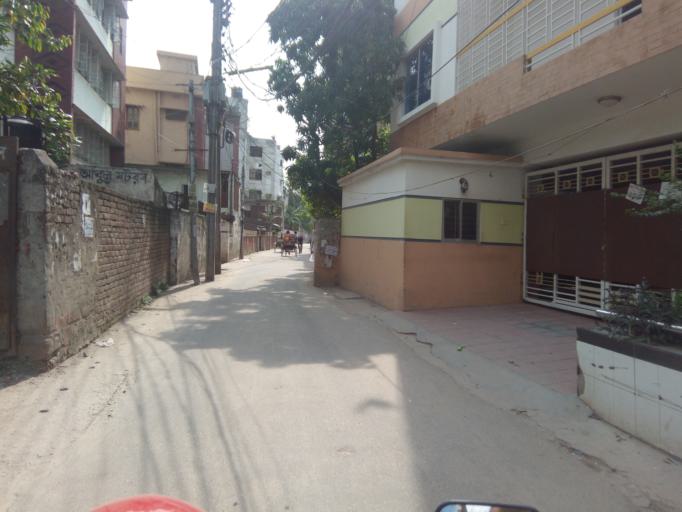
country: BD
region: Dhaka
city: Paltan
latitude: 23.7497
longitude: 90.3987
